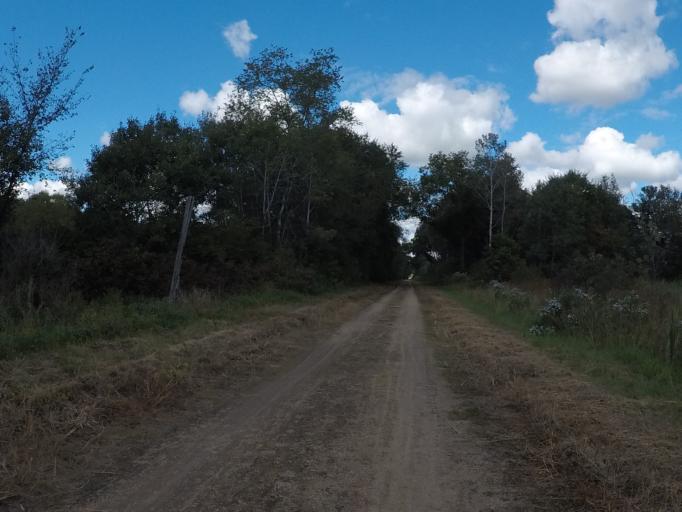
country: US
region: Wisconsin
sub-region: Richland County
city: Richland Center
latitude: 43.3028
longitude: -90.3381
